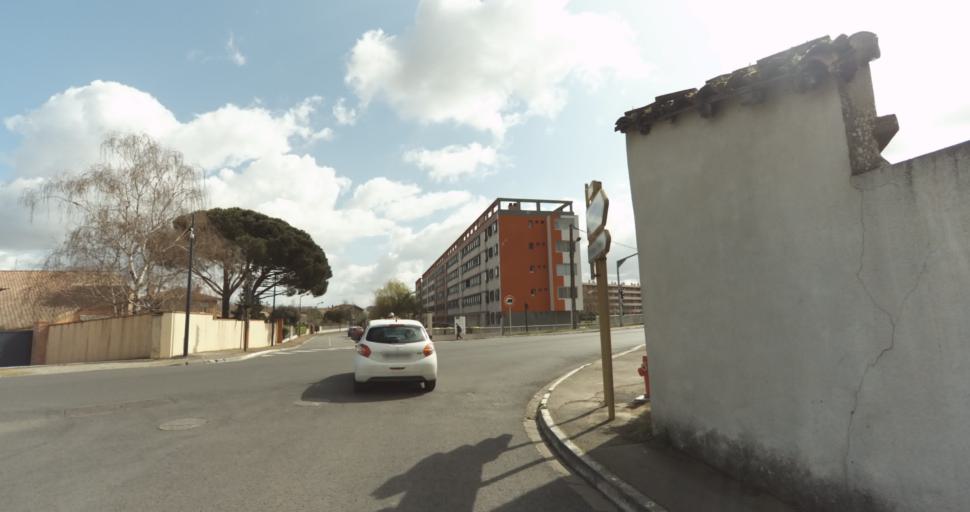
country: FR
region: Midi-Pyrenees
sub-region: Departement de la Haute-Garonne
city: Auterive
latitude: 43.3545
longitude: 1.4682
